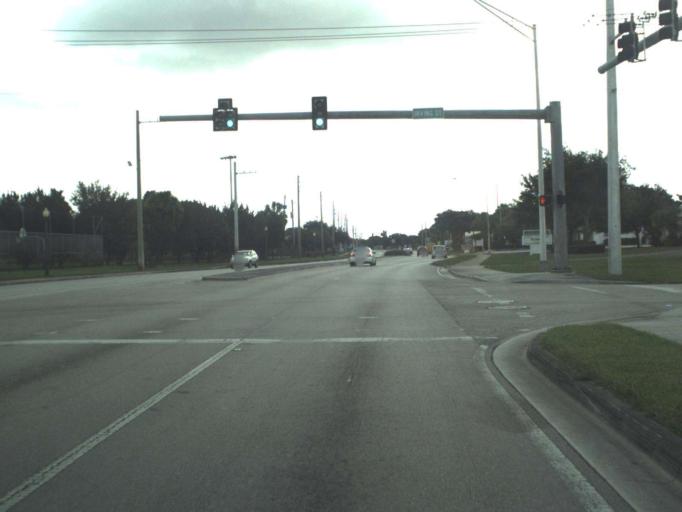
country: US
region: Florida
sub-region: Saint Lucie County
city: River Park
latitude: 27.3177
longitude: -80.3537
